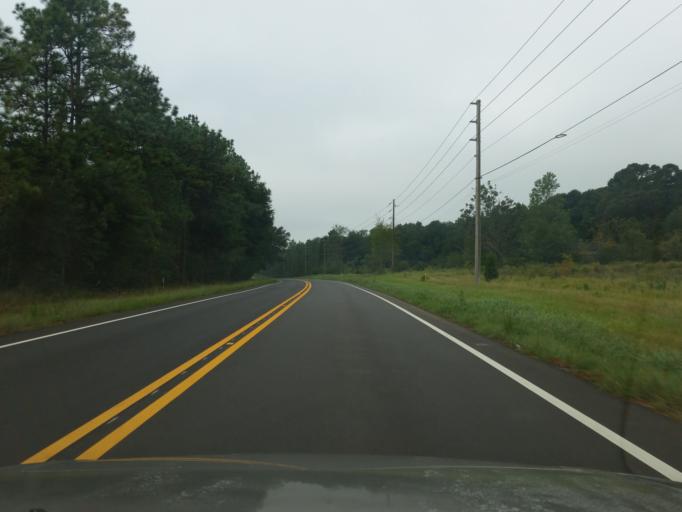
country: US
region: Alabama
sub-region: Baldwin County
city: Bay Minette
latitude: 30.8177
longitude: -87.8643
